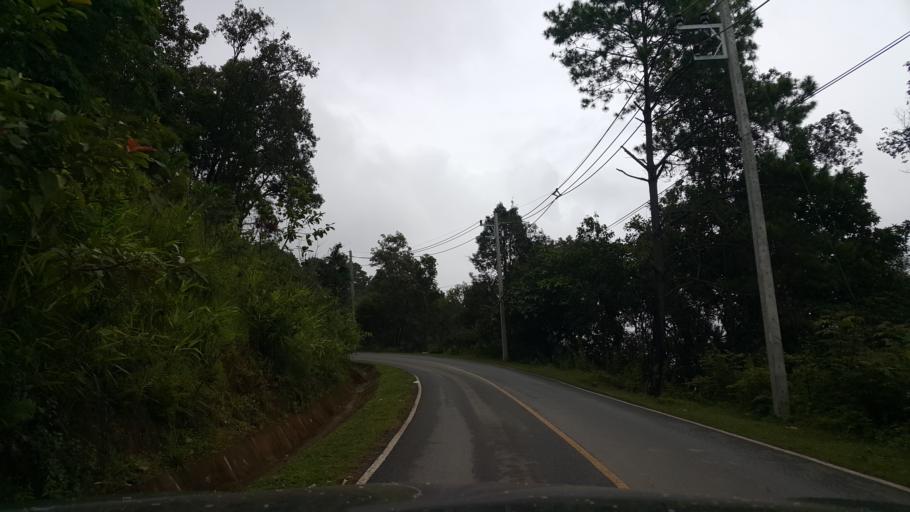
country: TH
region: Chiang Mai
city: Samoeng
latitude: 18.8847
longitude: 98.5352
